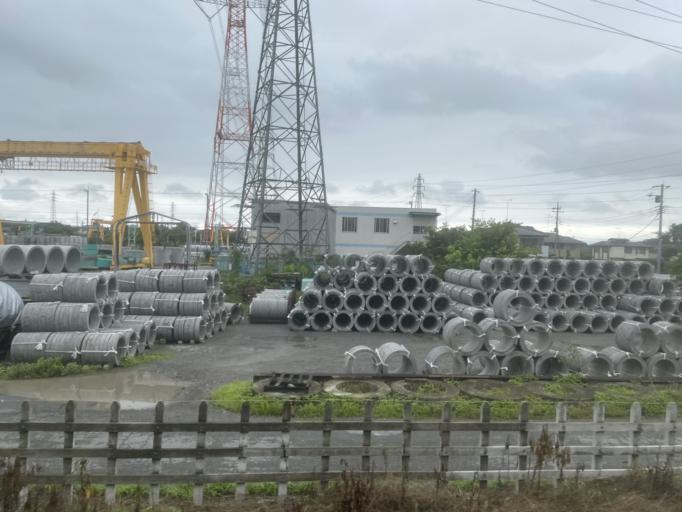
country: JP
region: Saitama
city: Kumagaya
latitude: 36.1450
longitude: 139.3358
